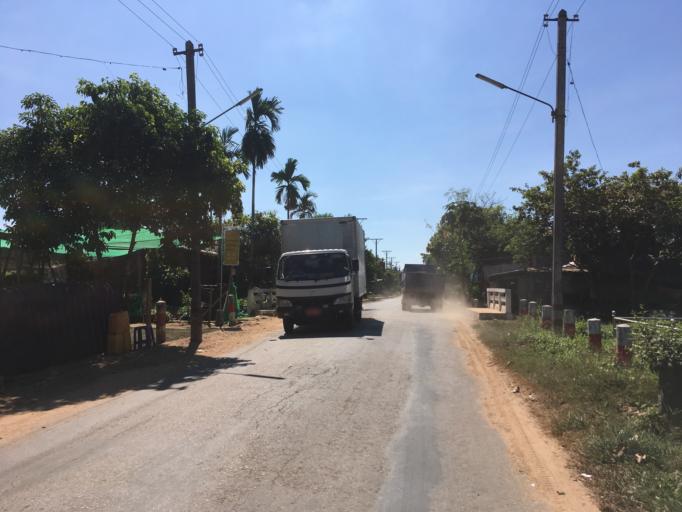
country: MM
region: Mon
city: Kyaikkami
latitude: 15.5065
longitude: 97.8390
